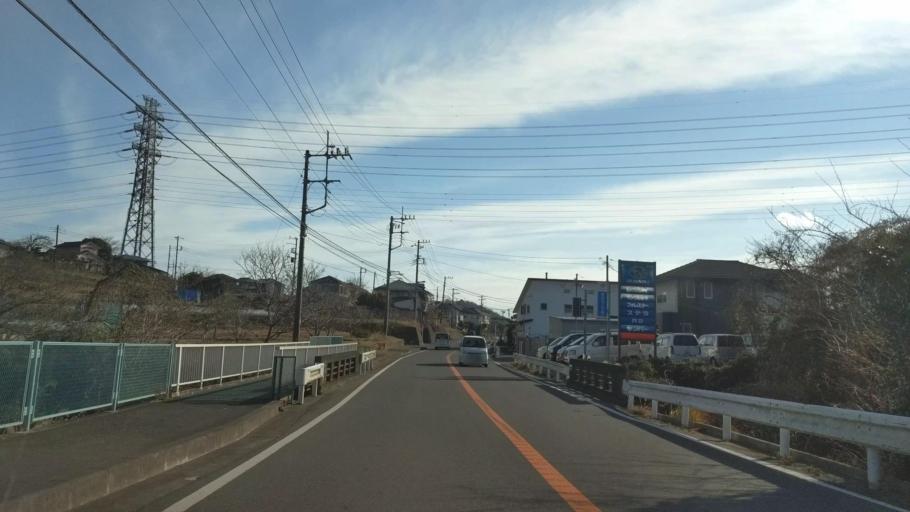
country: JP
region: Kanagawa
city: Hadano
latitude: 35.3898
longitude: 139.2352
